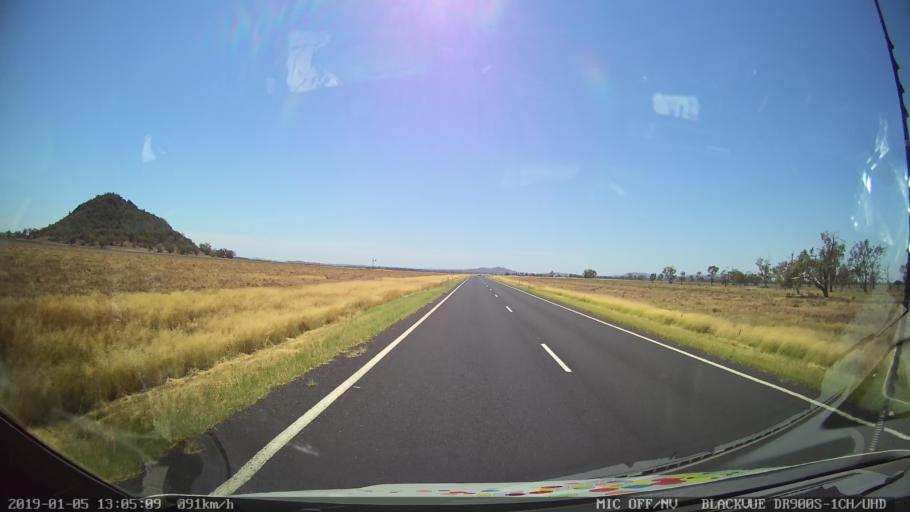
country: AU
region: New South Wales
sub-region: Gunnedah
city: Gunnedah
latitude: -31.0976
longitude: 149.8493
